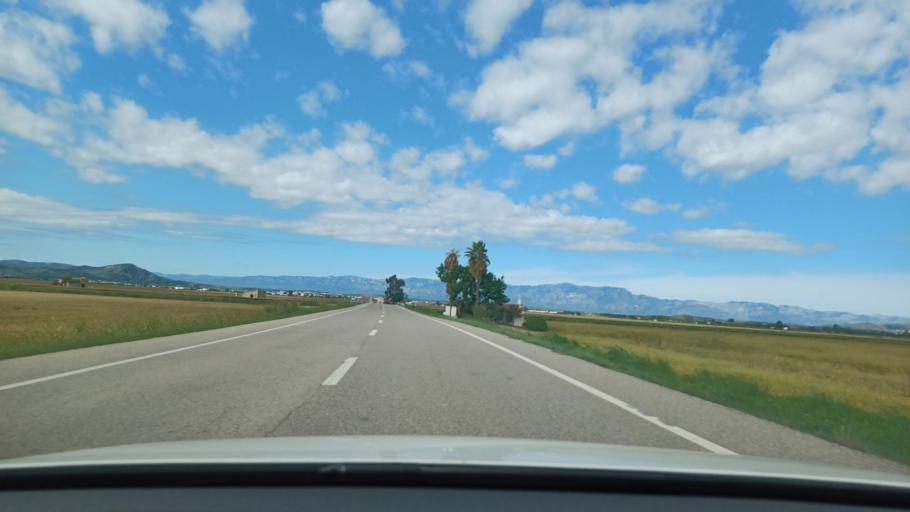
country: ES
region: Catalonia
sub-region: Provincia de Tarragona
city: Deltebre
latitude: 40.7028
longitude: 0.6654
